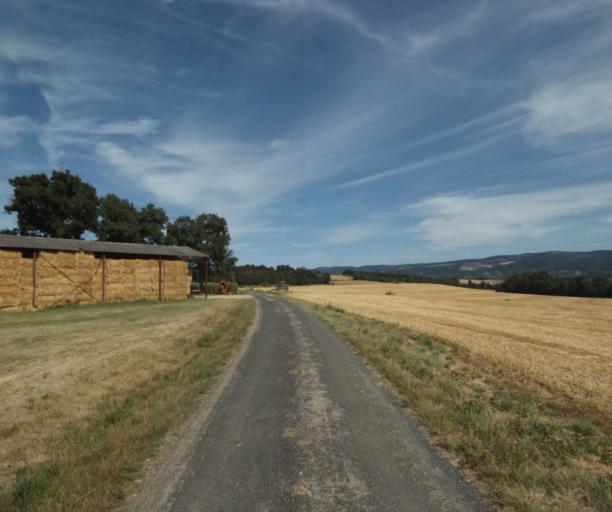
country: FR
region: Midi-Pyrenees
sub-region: Departement du Tarn
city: Soreze
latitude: 43.5100
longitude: 2.0767
